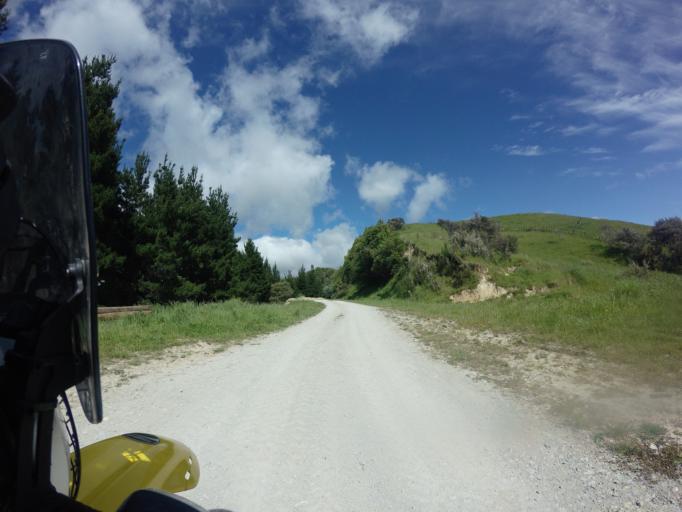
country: NZ
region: Hawke's Bay
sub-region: Wairoa District
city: Wairoa
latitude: -38.6650
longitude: 177.4862
